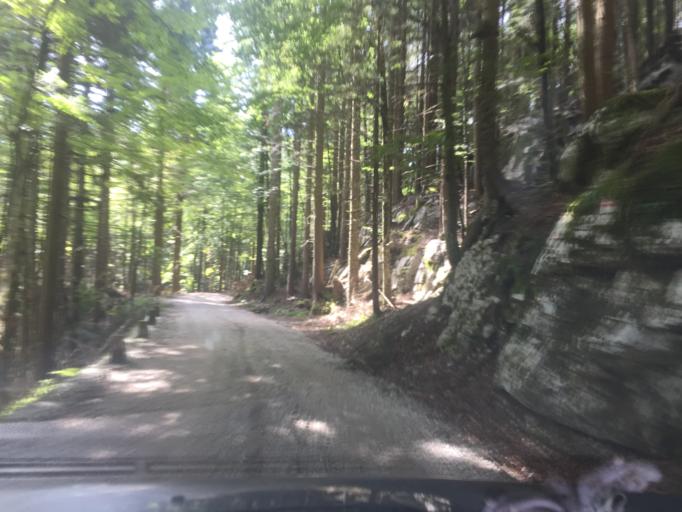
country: SI
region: Ajdovscina
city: Lokavec
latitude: 45.9846
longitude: 13.8374
